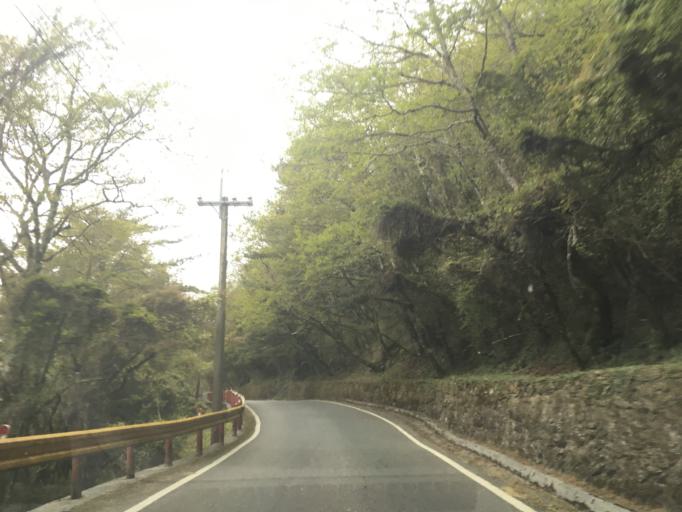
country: TW
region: Taiwan
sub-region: Hualien
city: Hualian
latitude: 24.1810
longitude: 121.3193
